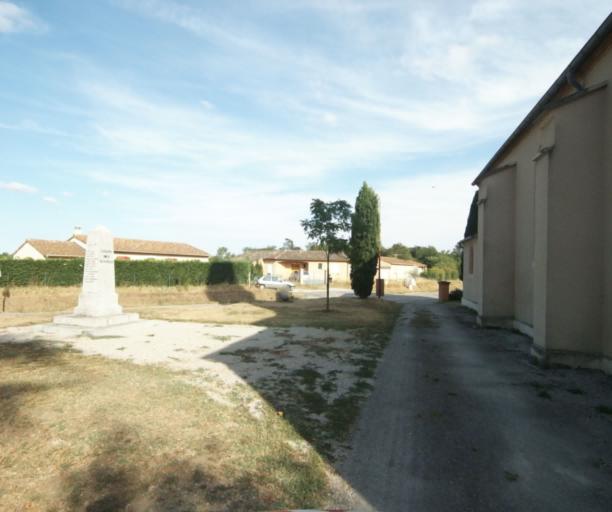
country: FR
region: Midi-Pyrenees
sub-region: Departement de la Haute-Garonne
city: Revel
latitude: 43.5041
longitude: 1.9976
